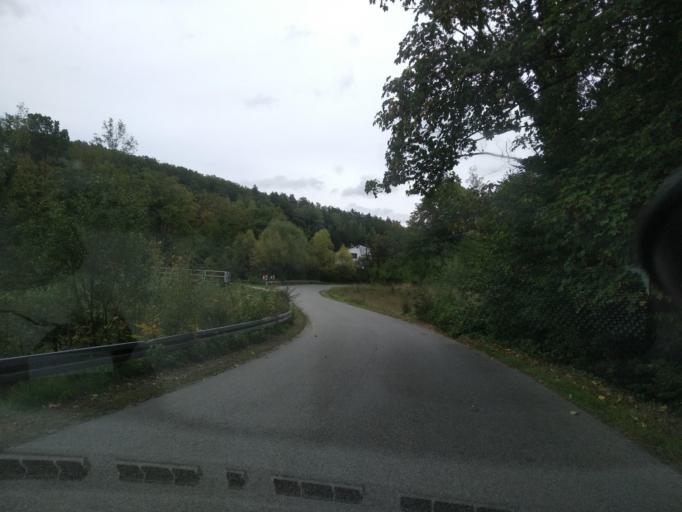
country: PL
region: Lesser Poland Voivodeship
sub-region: Powiat gorlicki
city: Sekowa
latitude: 49.6150
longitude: 21.2145
